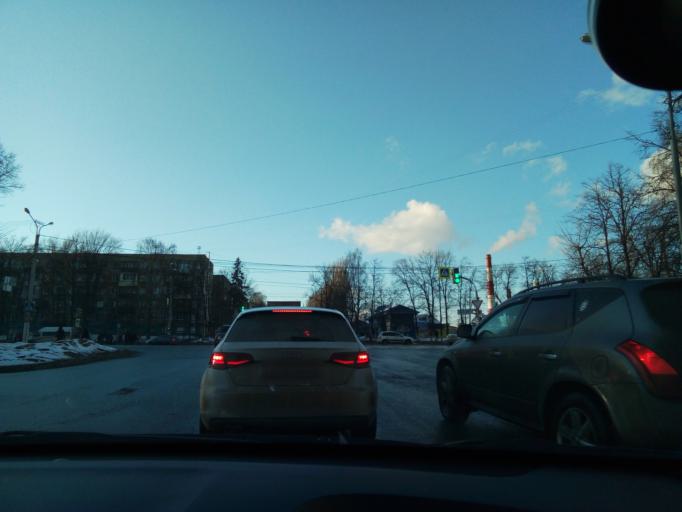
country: RU
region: Chuvashia
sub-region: Cheboksarskiy Rayon
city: Cheboksary
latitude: 56.1404
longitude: 47.1987
